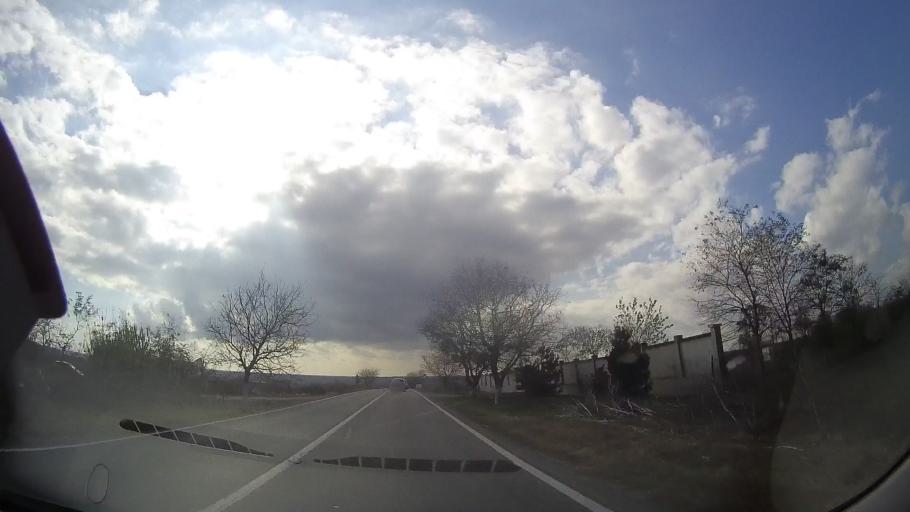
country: RO
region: Constanta
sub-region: Oras Techirghiol
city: Techirghiol
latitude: 44.0713
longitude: 28.5966
